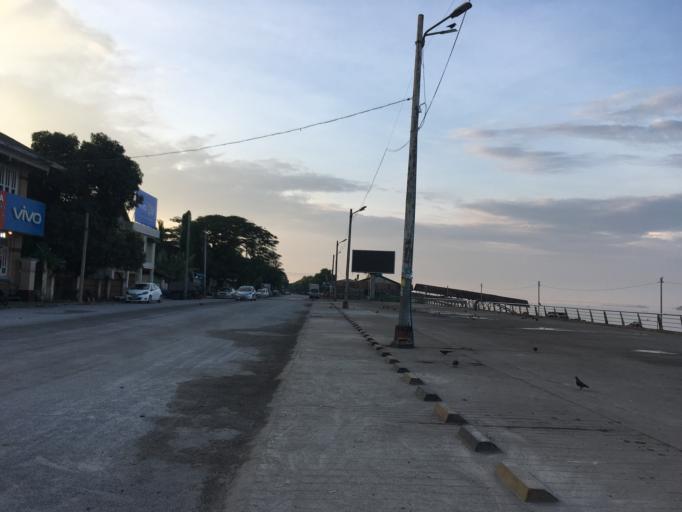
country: MM
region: Mon
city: Mawlamyine
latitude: 16.4823
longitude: 97.6186
